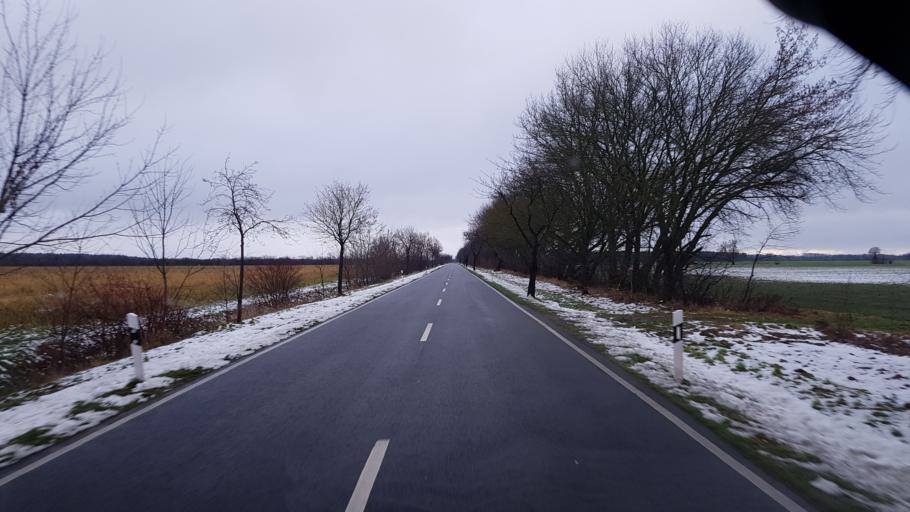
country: DE
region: Brandenburg
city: Luckau
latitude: 51.8501
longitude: 13.7647
